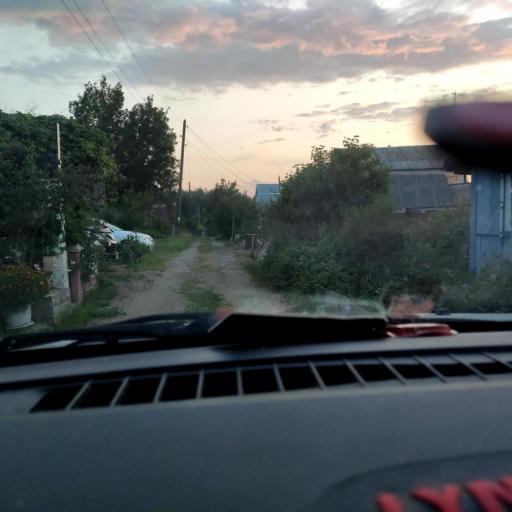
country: RU
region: Perm
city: Kukushtan
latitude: 57.6186
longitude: 56.4716
